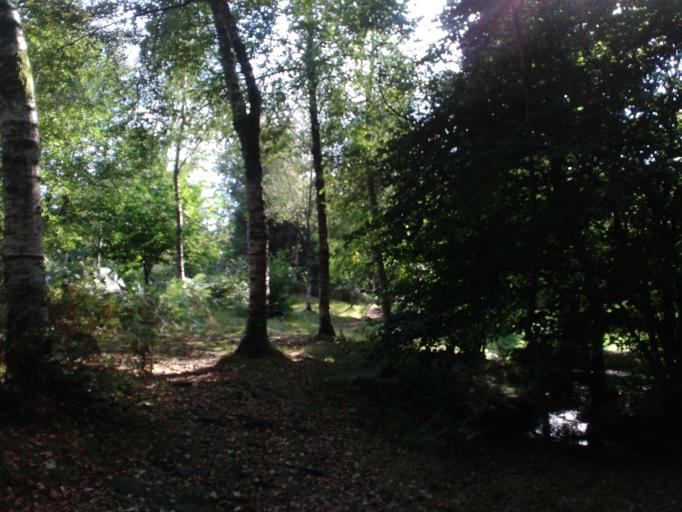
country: ES
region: Galicia
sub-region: Provincia de Pontevedra
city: Marin
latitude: 42.3607
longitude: -8.6755
